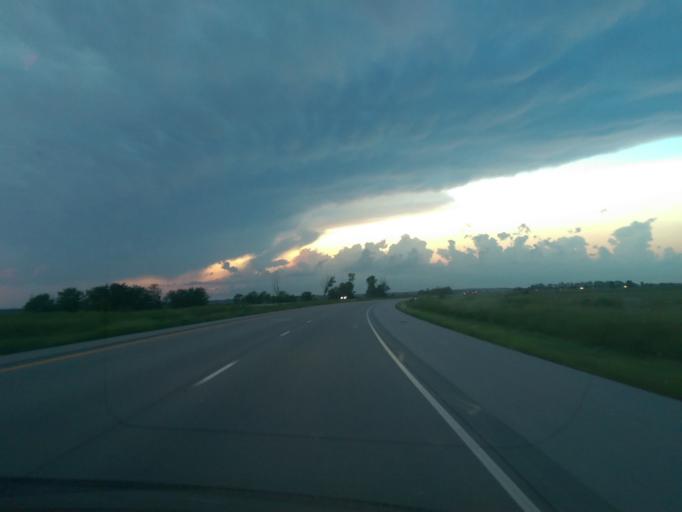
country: US
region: Nebraska
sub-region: Otoe County
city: Nebraska City
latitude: 40.7263
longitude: -95.8156
